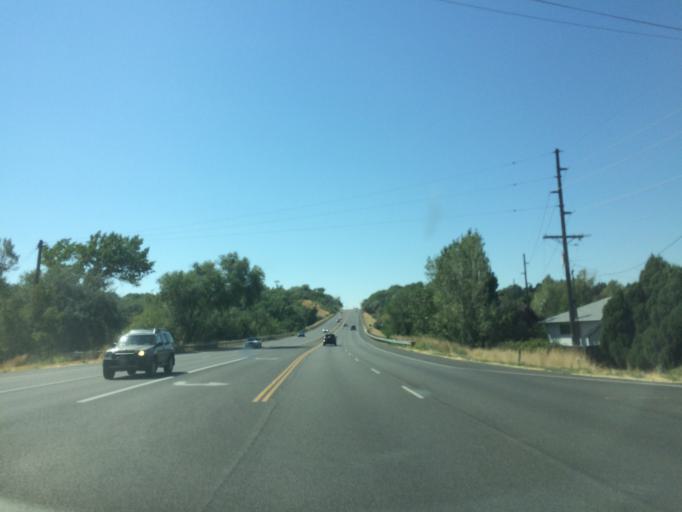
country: US
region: Utah
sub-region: Weber County
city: Ogden
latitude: 41.2388
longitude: -111.9457
